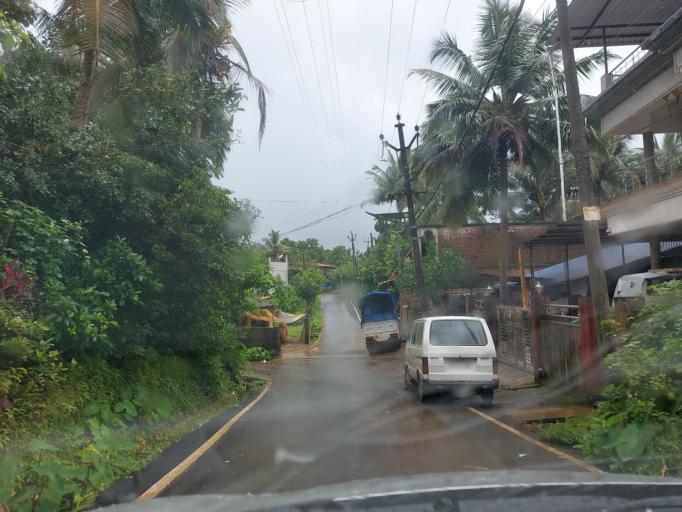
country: IN
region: Goa
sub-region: North Goa
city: Valpoy
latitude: 15.5328
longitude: 74.1295
